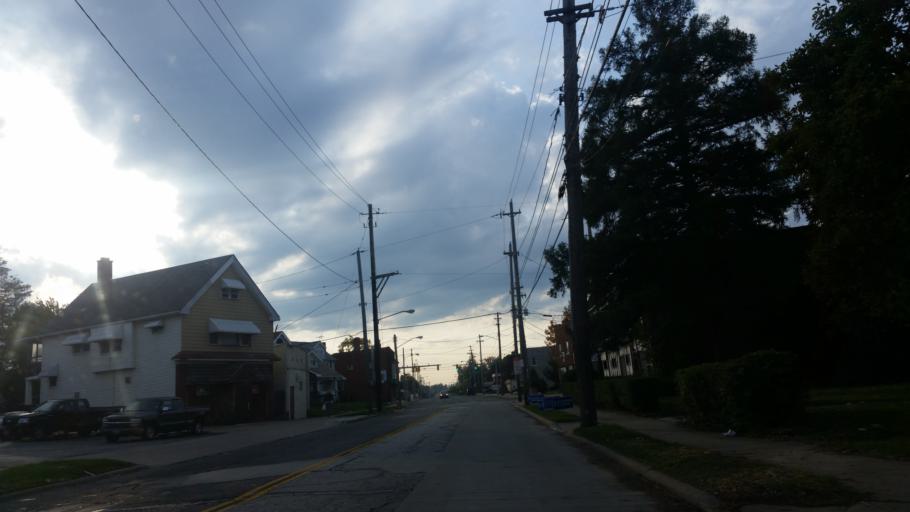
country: US
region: Ohio
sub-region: Cuyahoga County
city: Garfield Heights
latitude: 41.4350
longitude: -81.6194
